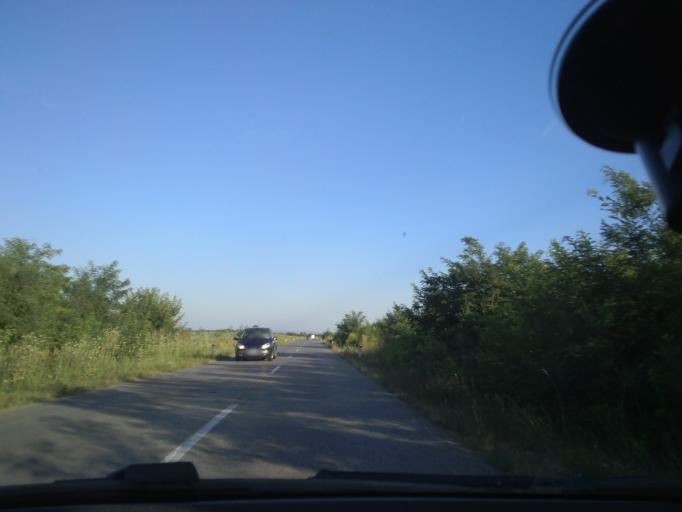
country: RS
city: Obrovac
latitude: 45.4324
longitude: 19.3802
